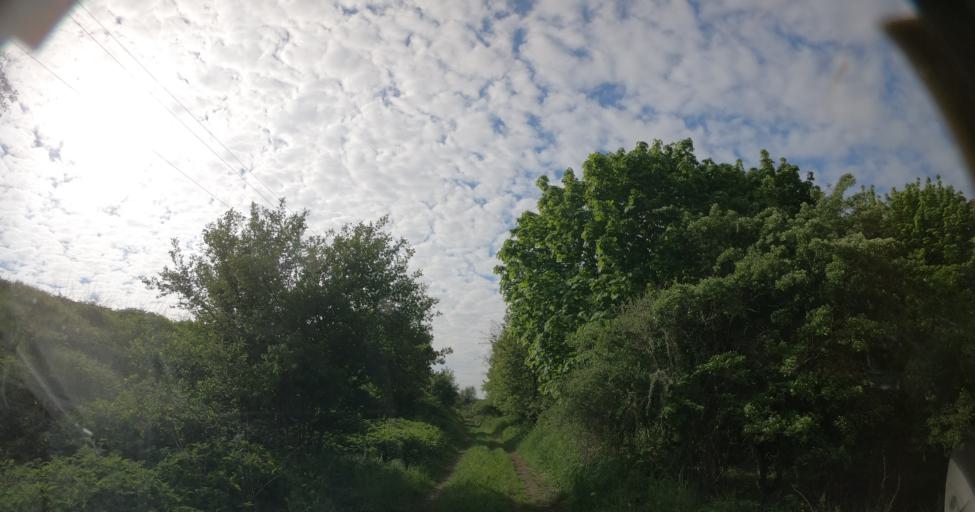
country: PL
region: West Pomeranian Voivodeship
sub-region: Powiat stargardzki
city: Stargard Szczecinski
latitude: 53.3432
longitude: 15.0626
